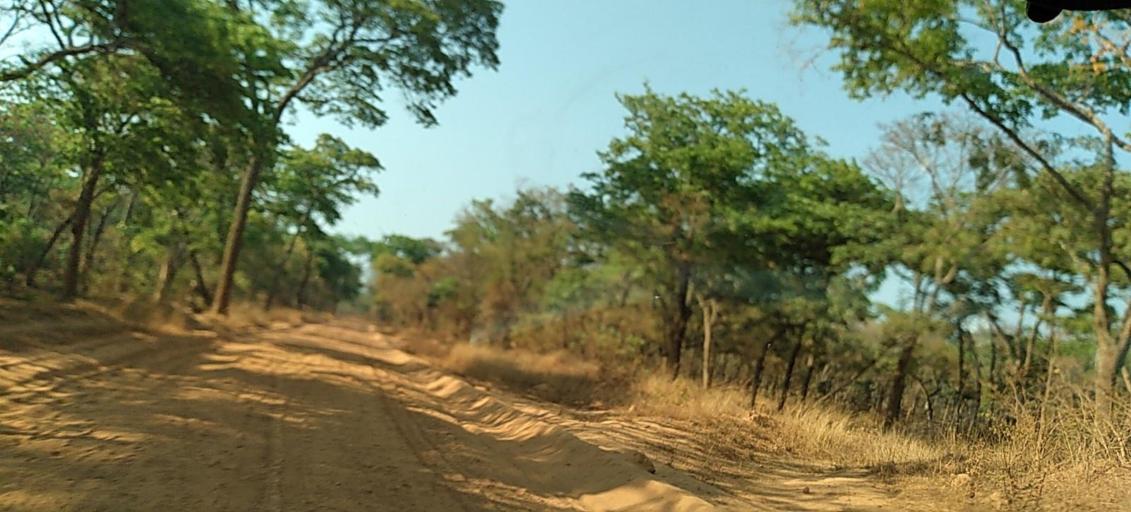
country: ZM
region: North-Western
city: Kasempa
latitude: -13.6120
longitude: 25.9787
